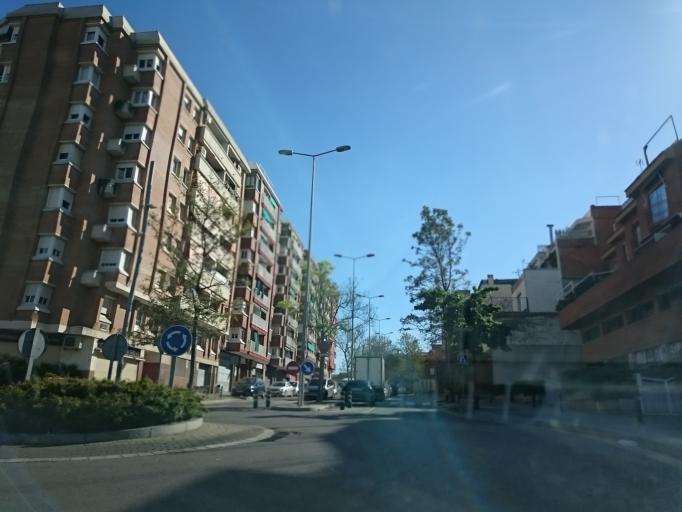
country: ES
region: Catalonia
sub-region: Provincia de Barcelona
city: Viladecans
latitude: 41.3233
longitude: 2.0109
